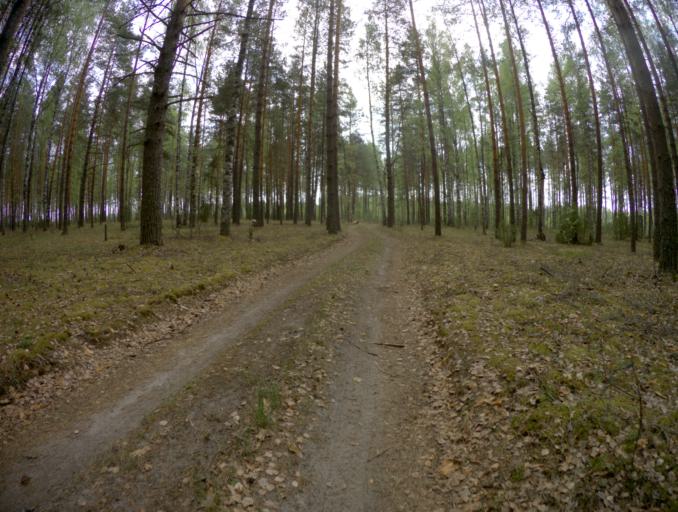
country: RU
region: Ivanovo
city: Talitsy
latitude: 56.4858
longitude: 42.1689
